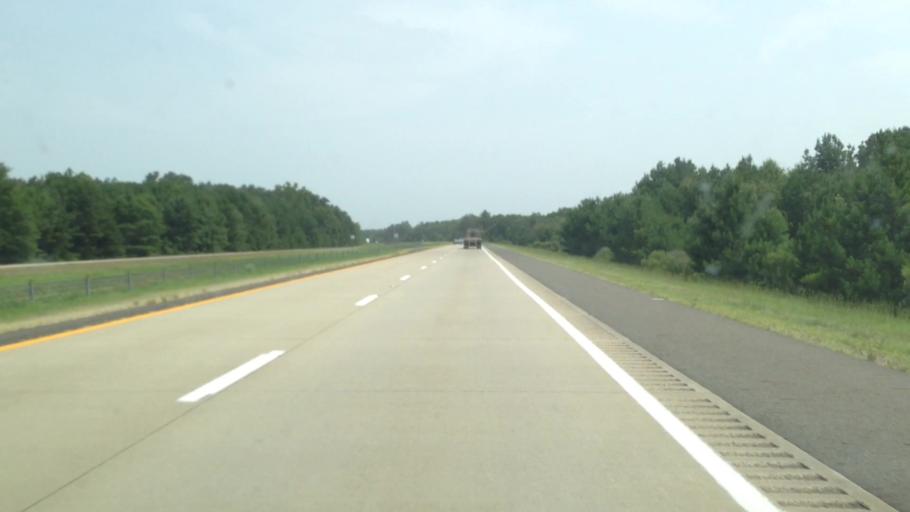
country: US
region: Texas
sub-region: Bowie County
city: Texarkana
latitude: 33.2070
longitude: -93.8754
